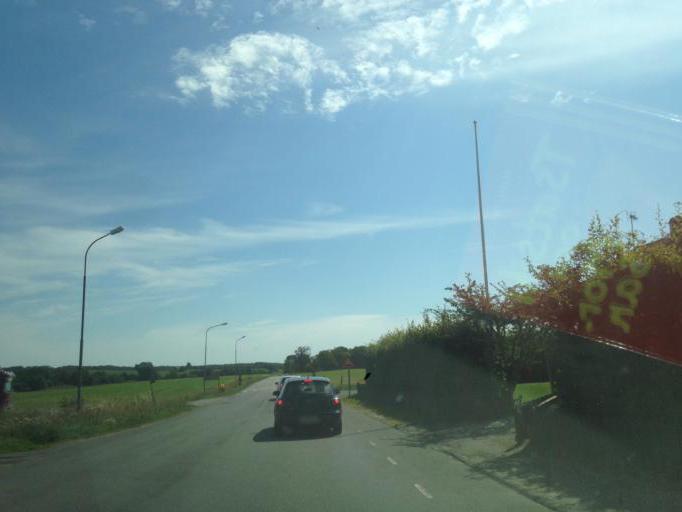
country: SE
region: Skane
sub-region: Simrishamns Kommun
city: Kivik
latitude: 55.6368
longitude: 14.1360
